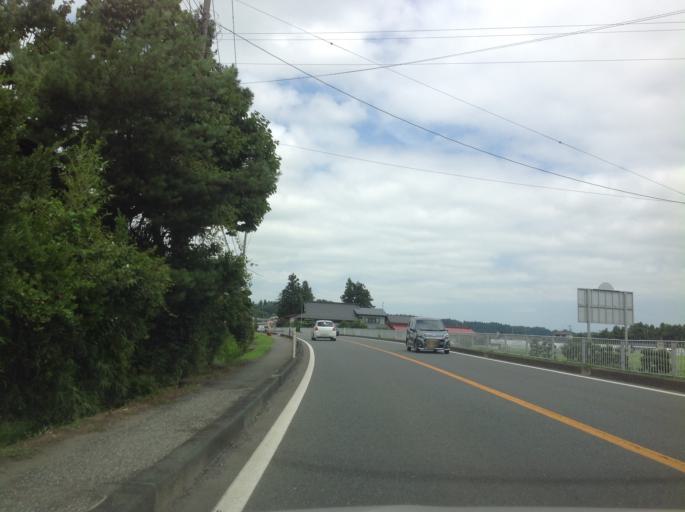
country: JP
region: Iwate
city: Mizusawa
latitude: 39.0881
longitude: 141.1367
